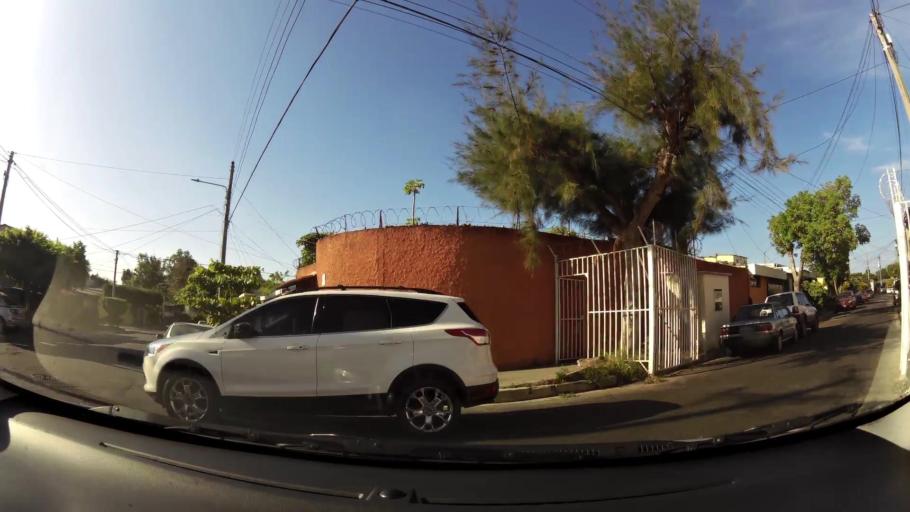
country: SV
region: La Libertad
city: Santa Tecla
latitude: 13.6810
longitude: -89.2844
